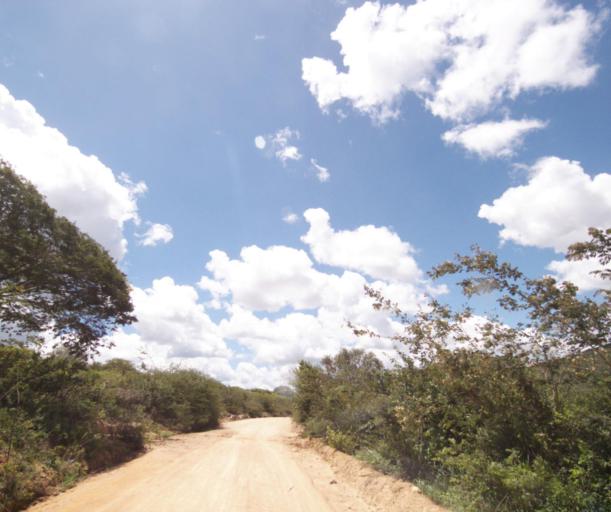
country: BR
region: Bahia
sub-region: Pocoes
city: Pocoes
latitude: -14.3830
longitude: -40.5552
